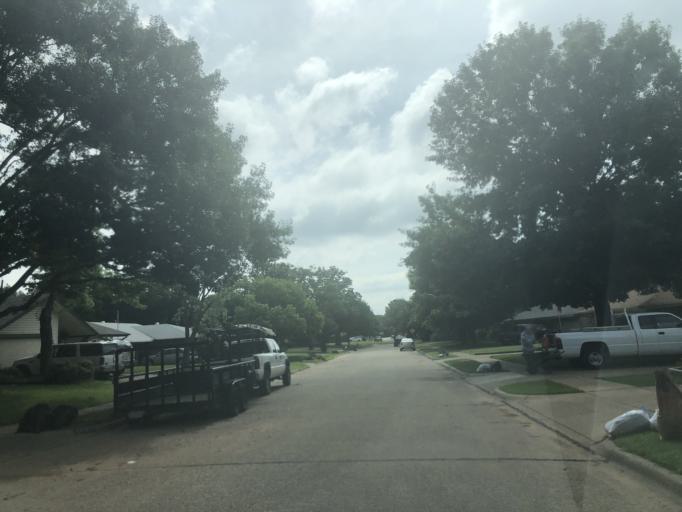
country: US
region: Texas
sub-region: Dallas County
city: Irving
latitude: 32.7975
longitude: -96.9733
